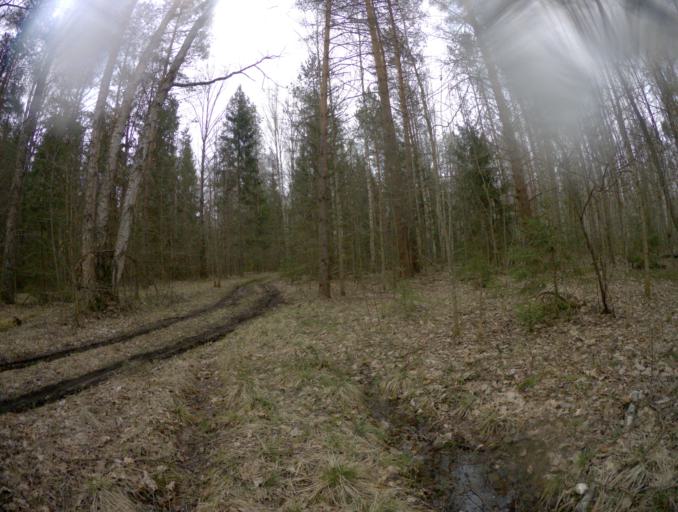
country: RU
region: Vladimir
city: Sudogda
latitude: 56.0279
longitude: 40.7938
